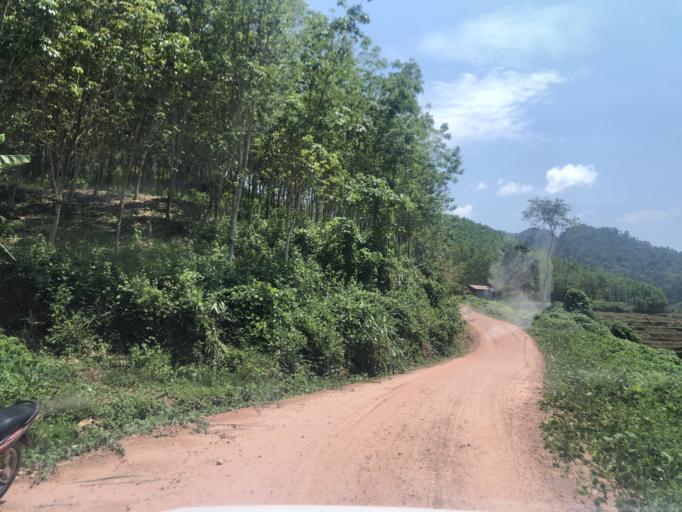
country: LA
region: Phongsali
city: Phongsali
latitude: 21.4218
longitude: 101.9805
